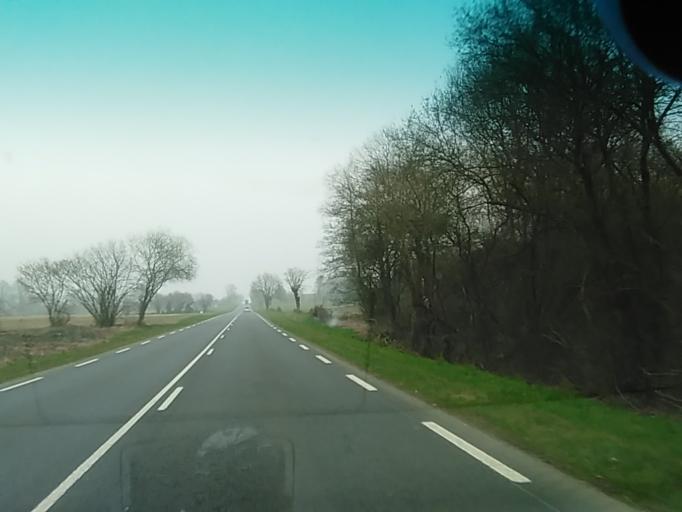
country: FR
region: Lower Normandy
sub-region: Departement de l'Orne
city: Magny-le-Desert
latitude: 48.6065
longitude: -0.3250
